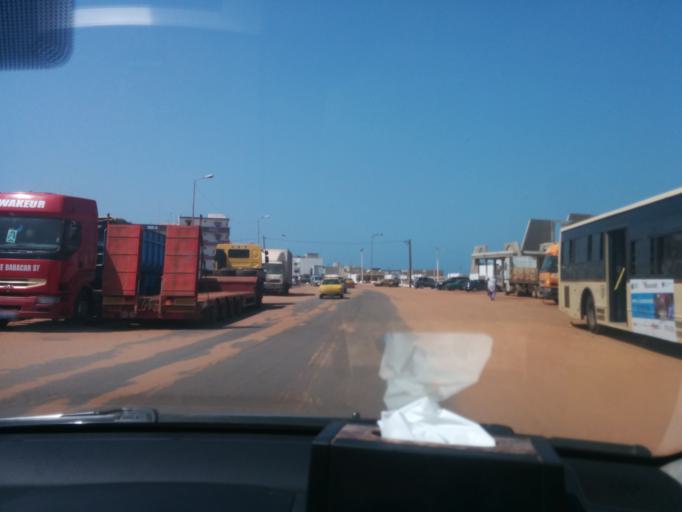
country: SN
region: Dakar
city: Pikine
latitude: 14.7708
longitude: -17.4254
